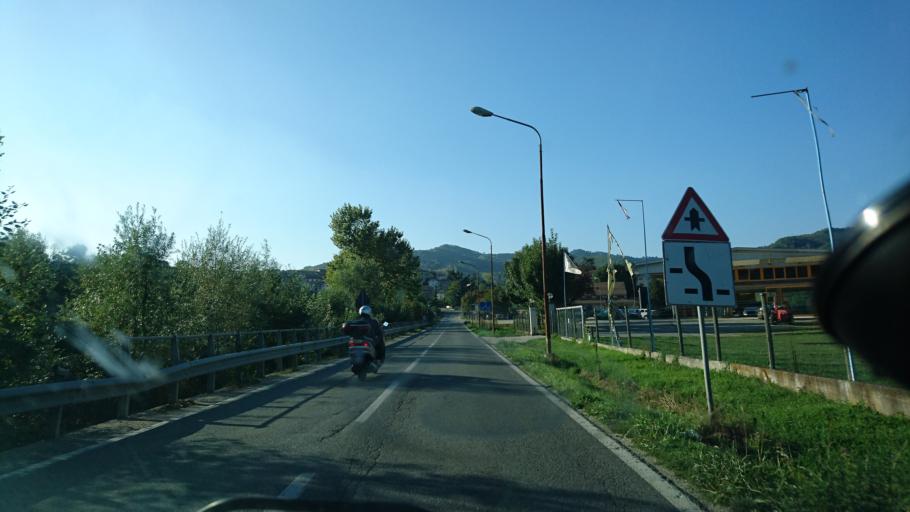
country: IT
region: Piedmont
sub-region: Provincia di Asti
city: Bubbio
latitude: 44.6613
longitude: 8.3018
